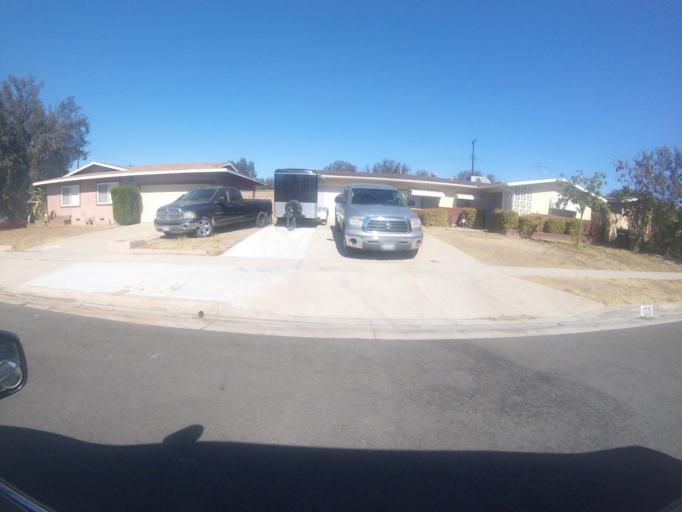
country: US
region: California
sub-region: San Bernardino County
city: Redlands
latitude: 34.0787
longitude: -117.1811
